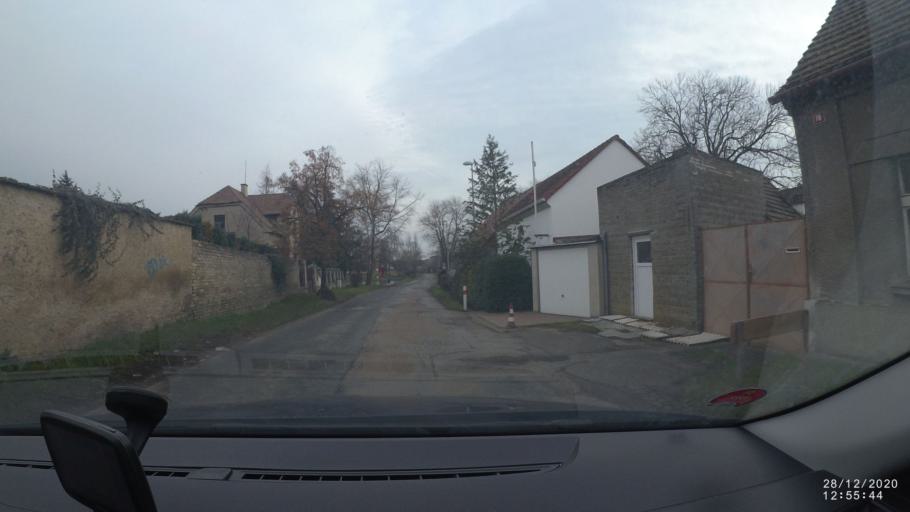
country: CZ
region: Praha
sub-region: Praha 19
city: Satalice
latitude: 50.1551
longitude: 14.5802
